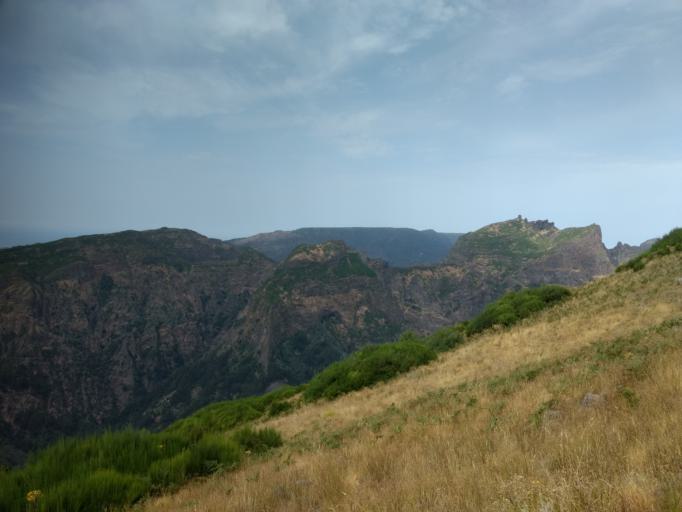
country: PT
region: Madeira
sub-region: Camara de Lobos
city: Curral das Freiras
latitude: 32.7192
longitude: -16.9540
